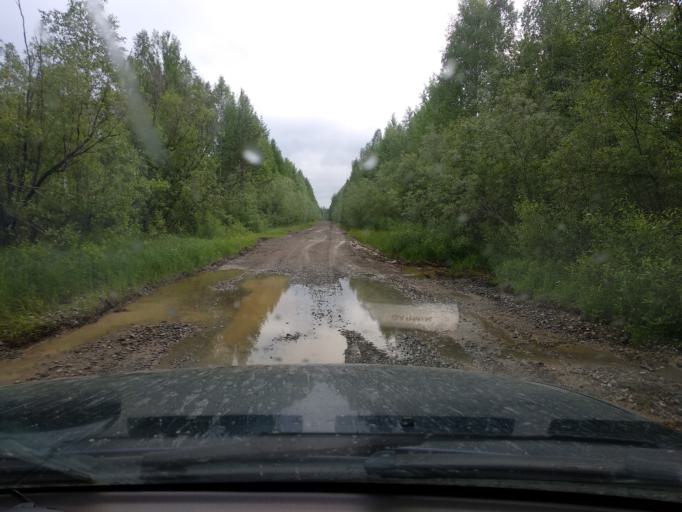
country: RU
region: Sverdlovsk
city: Karpinsk
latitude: 59.4274
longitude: 59.9642
